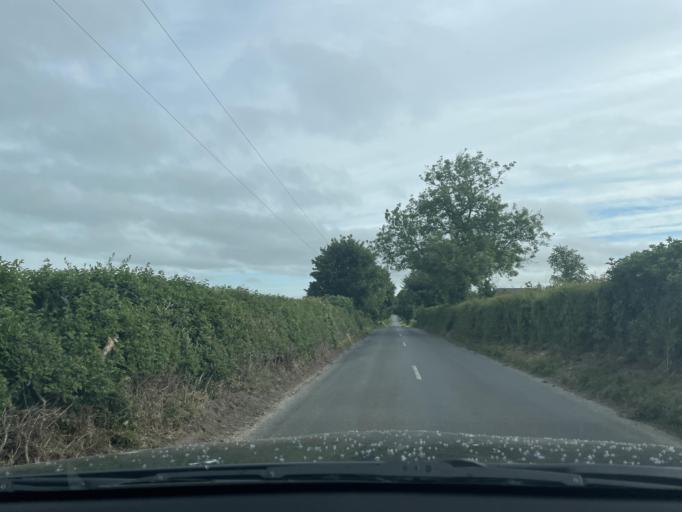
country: IE
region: Leinster
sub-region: County Carlow
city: Bagenalstown
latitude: 52.6414
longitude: -6.9730
